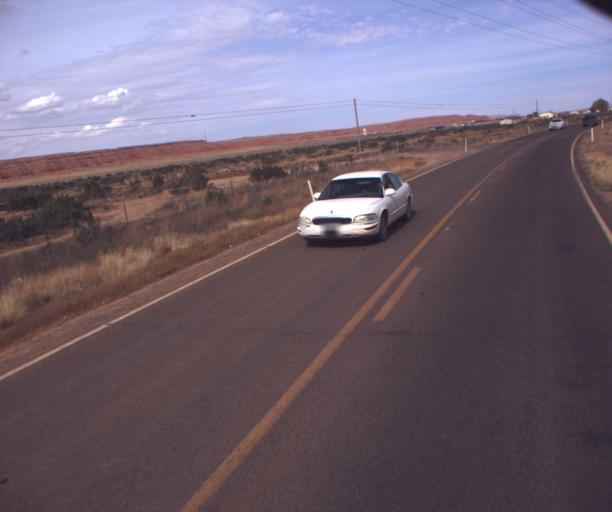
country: US
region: Arizona
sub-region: Apache County
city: Many Farms
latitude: 36.3366
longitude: -109.6245
